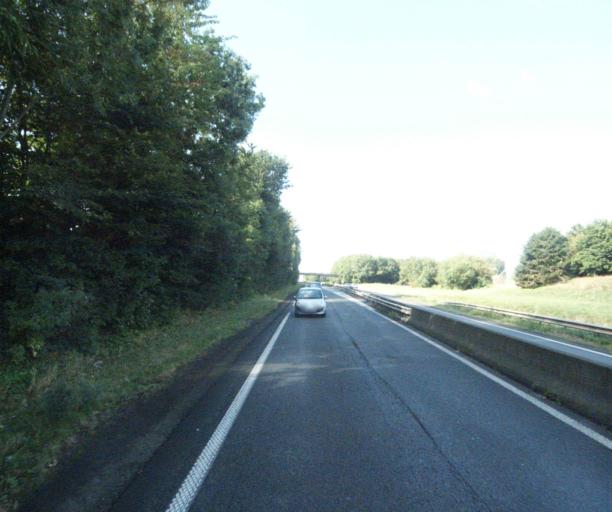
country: FR
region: Nord-Pas-de-Calais
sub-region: Departement du Nord
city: Lys-lez-Lannoy
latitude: 50.6587
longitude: 3.2149
